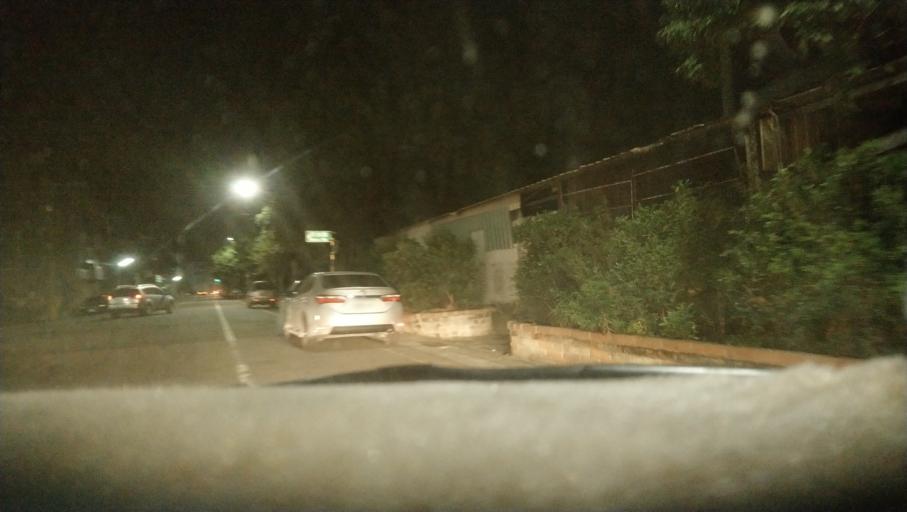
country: TW
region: Taiwan
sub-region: Yunlin
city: Douliu
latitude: 23.7113
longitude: 120.4413
